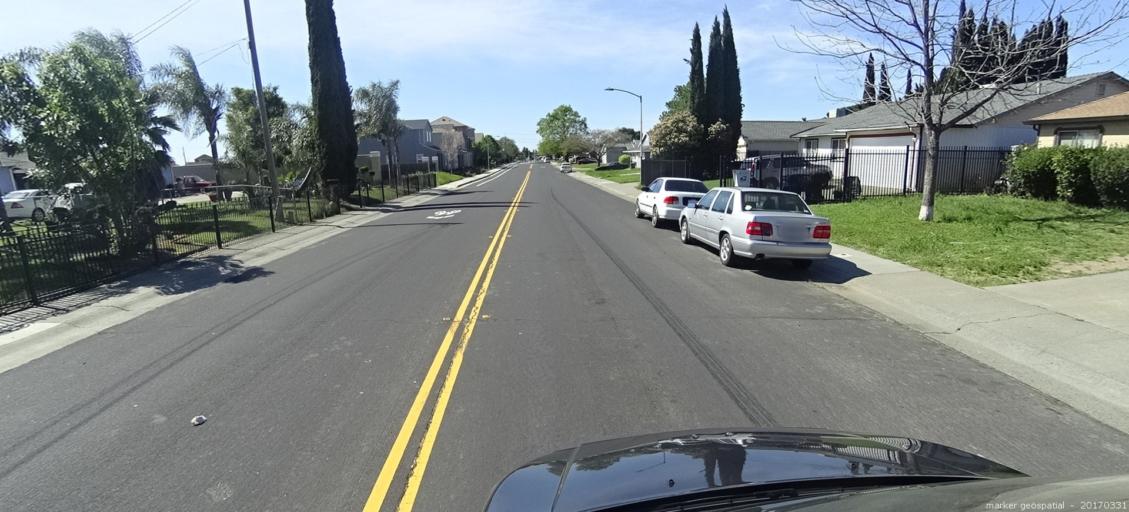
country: US
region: California
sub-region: Sacramento County
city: Parkway
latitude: 38.4598
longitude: -121.4419
